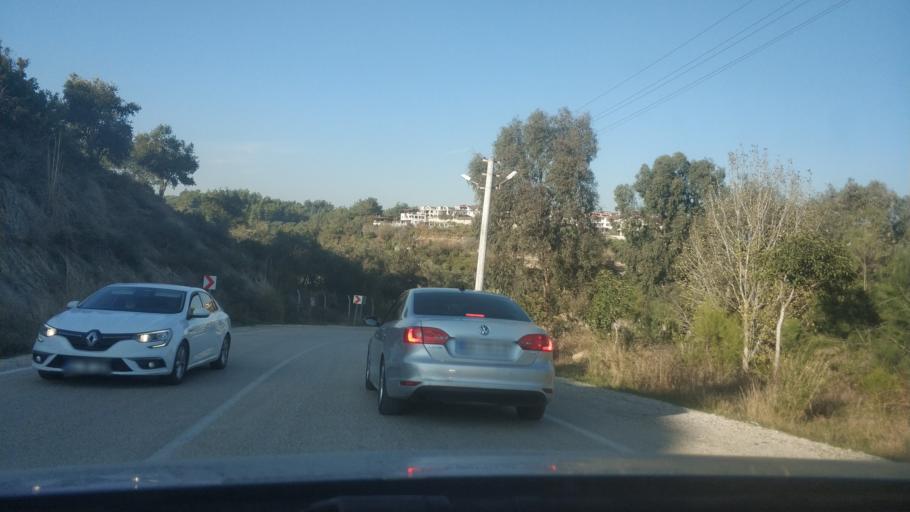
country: TR
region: Adana
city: Adana
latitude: 37.1037
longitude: 35.2946
